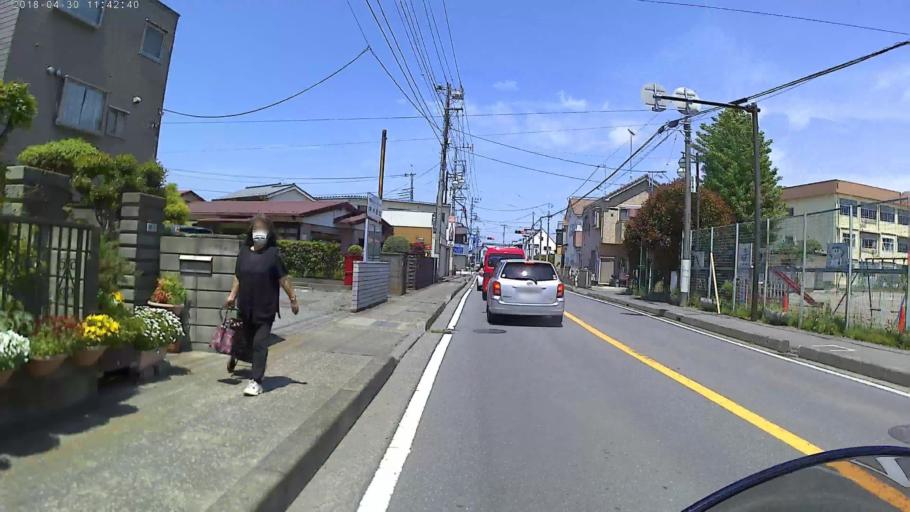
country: JP
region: Kanagawa
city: Zama
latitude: 35.4851
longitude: 139.3914
